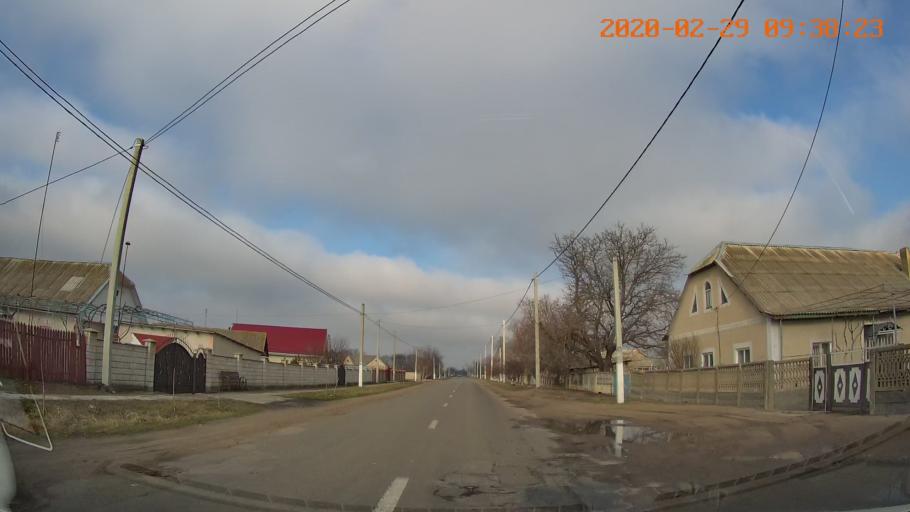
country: MD
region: Telenesti
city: Dnestrovsc
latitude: 46.6308
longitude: 29.8671
